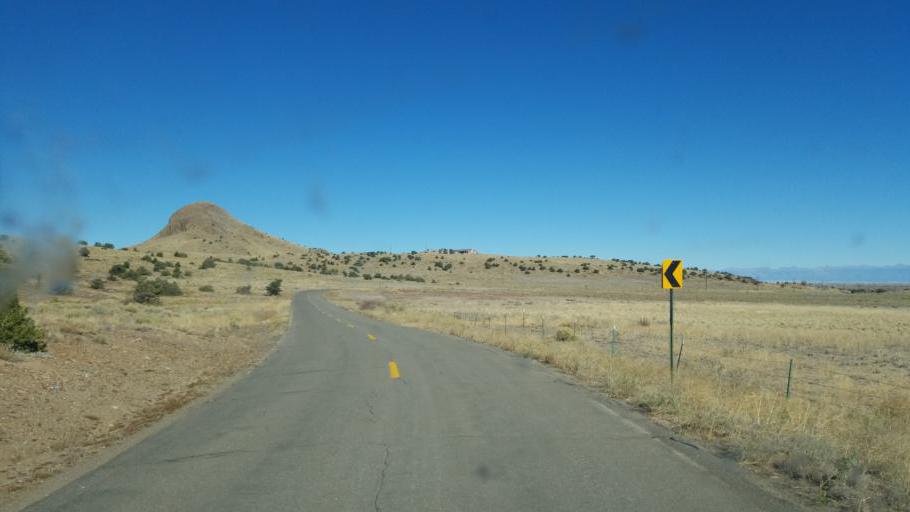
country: US
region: Colorado
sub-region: Rio Grande County
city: Del Norte
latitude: 37.6593
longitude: -106.3596
